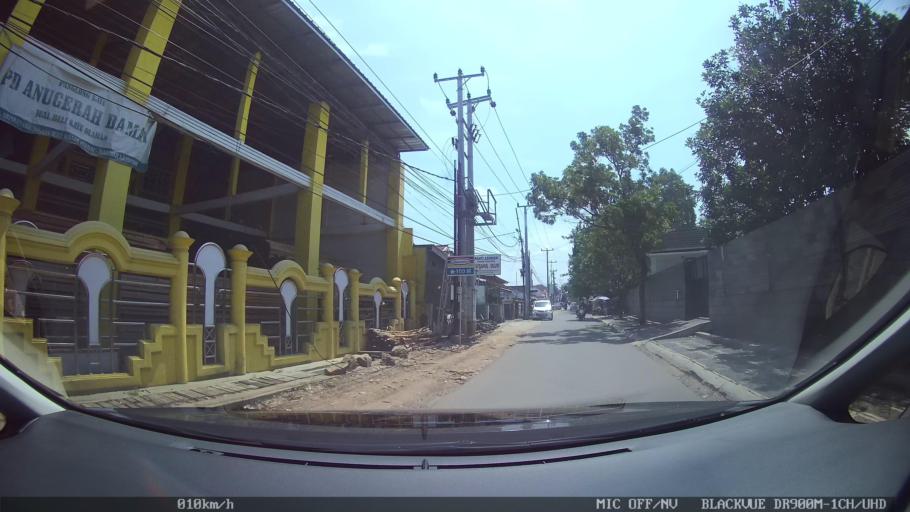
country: ID
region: Lampung
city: Kedaton
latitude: -5.3838
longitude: 105.2777
